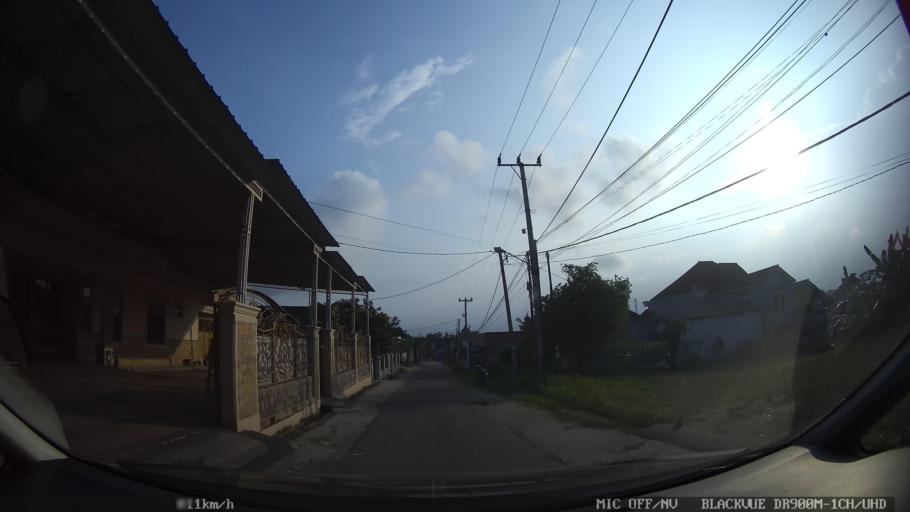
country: ID
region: Lampung
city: Kedaton
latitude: -5.3993
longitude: 105.2985
